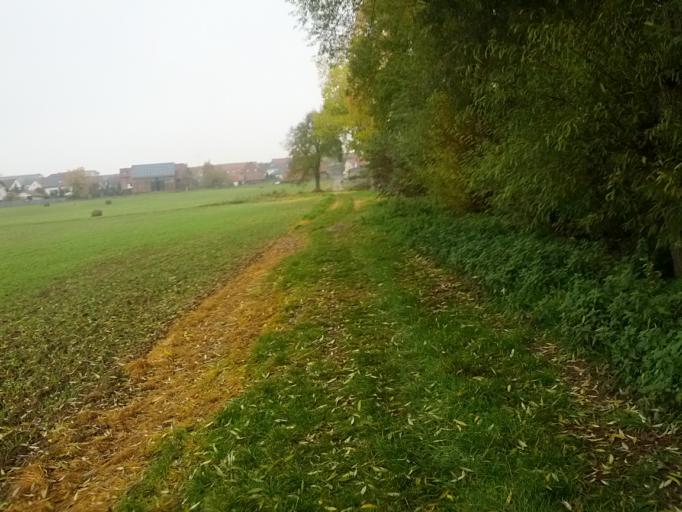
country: DE
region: Thuringia
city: Bischofroda
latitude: 50.9911
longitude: 10.4043
